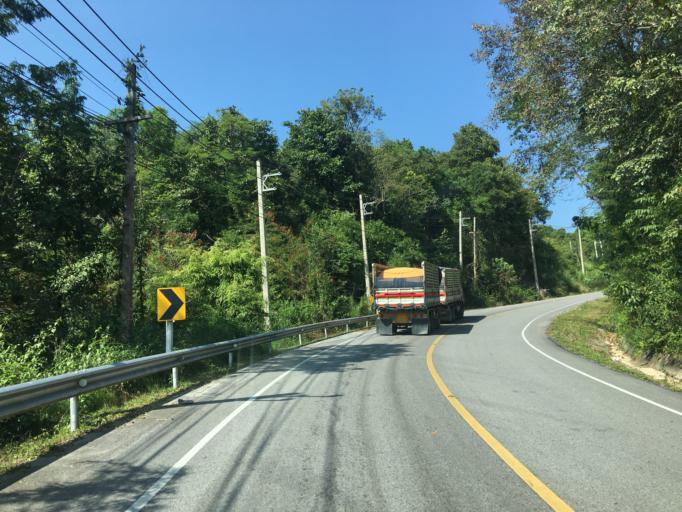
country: TH
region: Nan
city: Ban Luang
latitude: 18.8392
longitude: 100.3653
